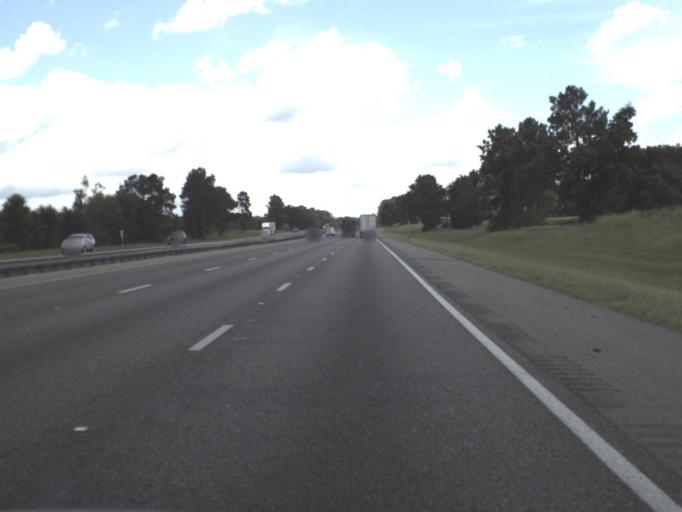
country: US
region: Florida
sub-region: Columbia County
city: Lake City
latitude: 30.0833
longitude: -82.6362
